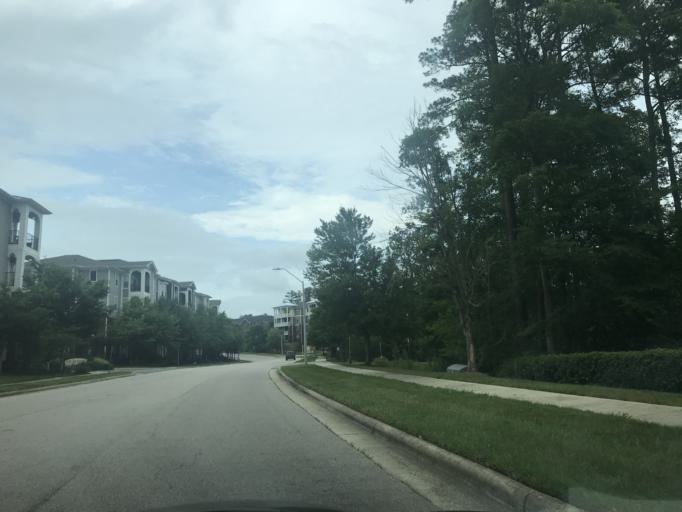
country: US
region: North Carolina
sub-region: Wake County
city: Green Level
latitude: 35.8204
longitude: -78.8992
